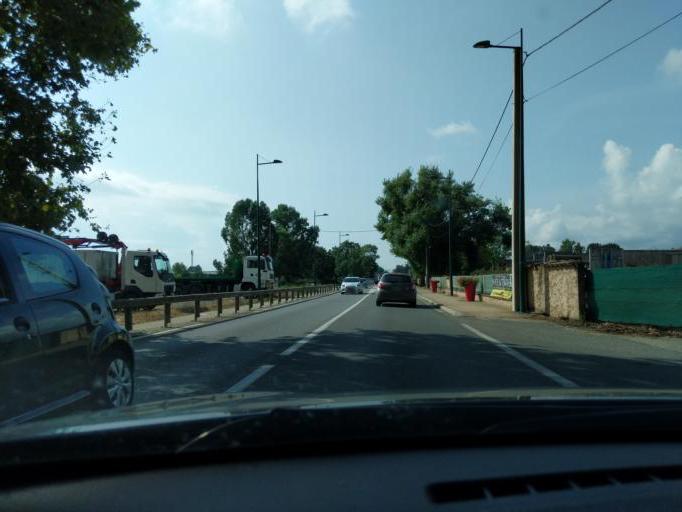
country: FR
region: Corsica
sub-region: Departement de la Haute-Corse
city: Ghisonaccia
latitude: 42.0048
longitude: 9.4031
